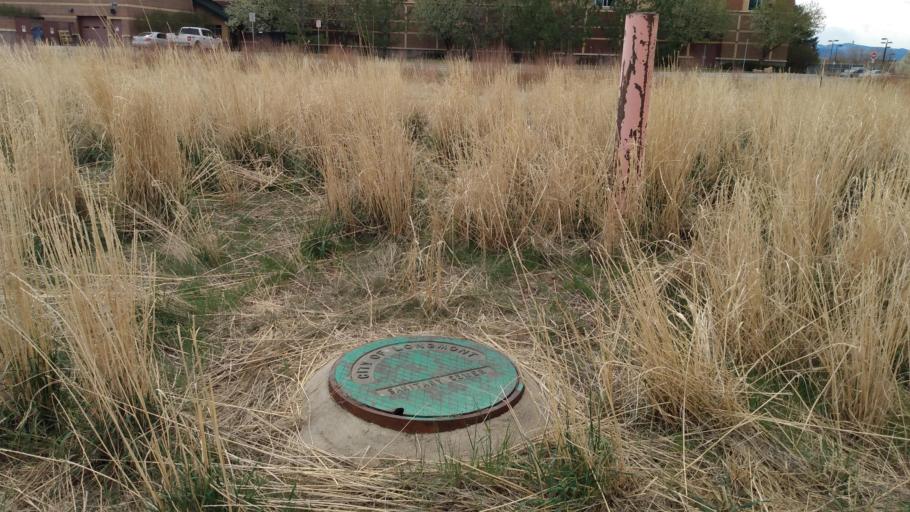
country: US
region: Colorado
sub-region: Boulder County
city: Longmont
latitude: 40.1463
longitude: -105.0961
